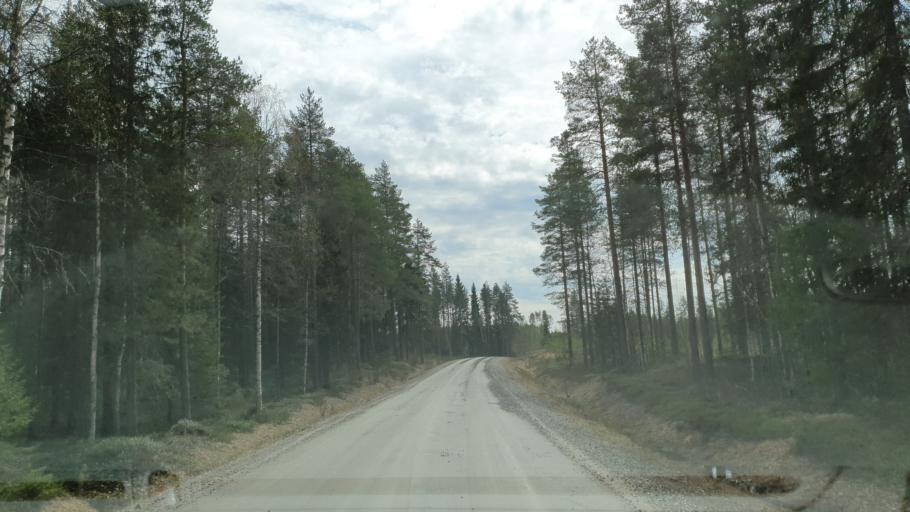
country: FI
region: Kainuu
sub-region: Kehys-Kainuu
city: Kuhmo
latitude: 64.1150
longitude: 29.9584
